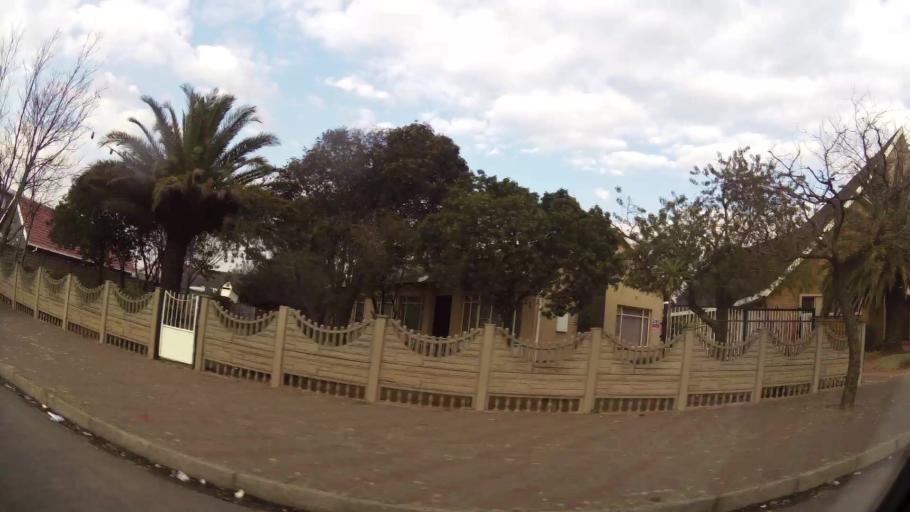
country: ZA
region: Gauteng
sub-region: Ekurhuleni Metropolitan Municipality
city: Germiston
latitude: -26.2377
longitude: 28.1962
